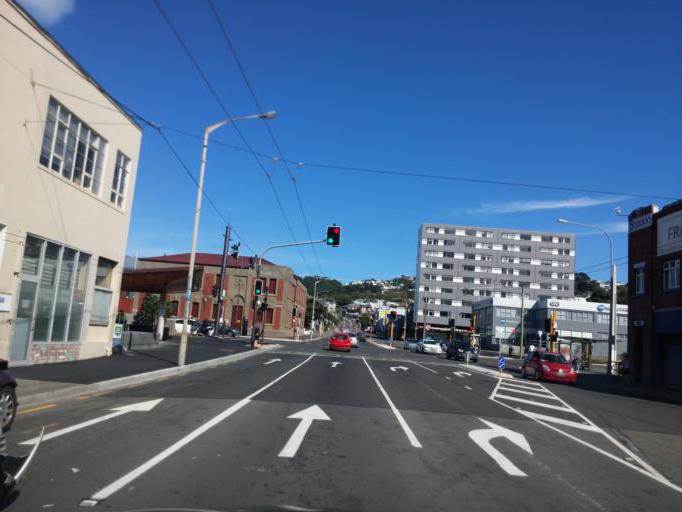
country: NZ
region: Wellington
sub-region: Wellington City
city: Wellington
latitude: -41.2974
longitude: 174.7761
